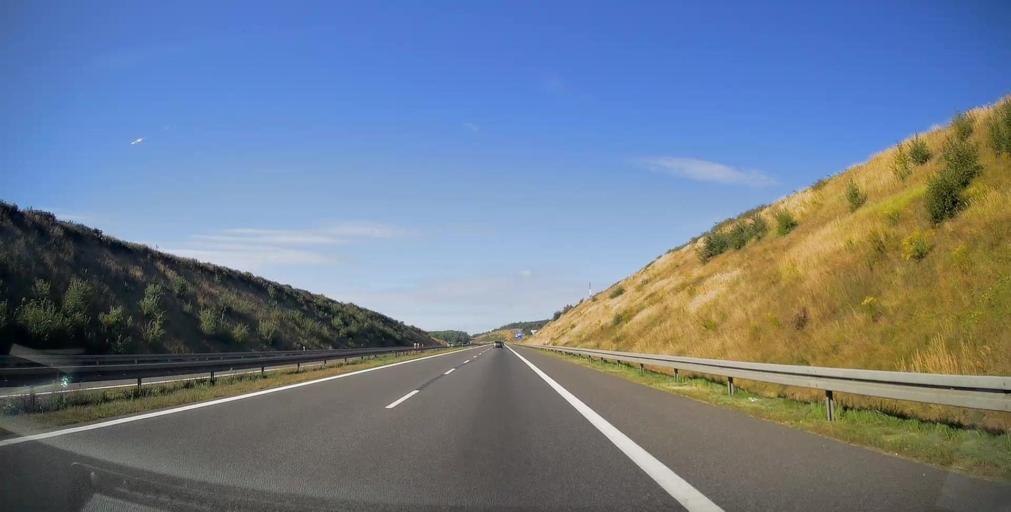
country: PL
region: Swietokrzyskie
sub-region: Powiat skarzyski
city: Laczna
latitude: 50.9884
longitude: 20.7662
